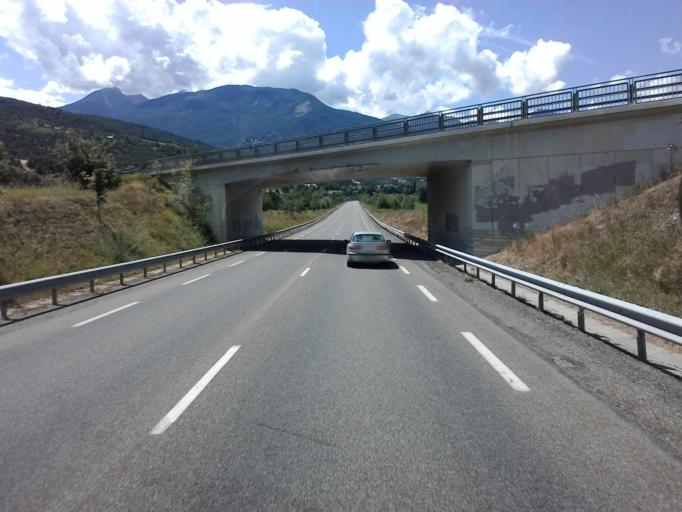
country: FR
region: Provence-Alpes-Cote d'Azur
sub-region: Departement des Hautes-Alpes
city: Embrun
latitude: 44.5636
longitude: 6.5072
